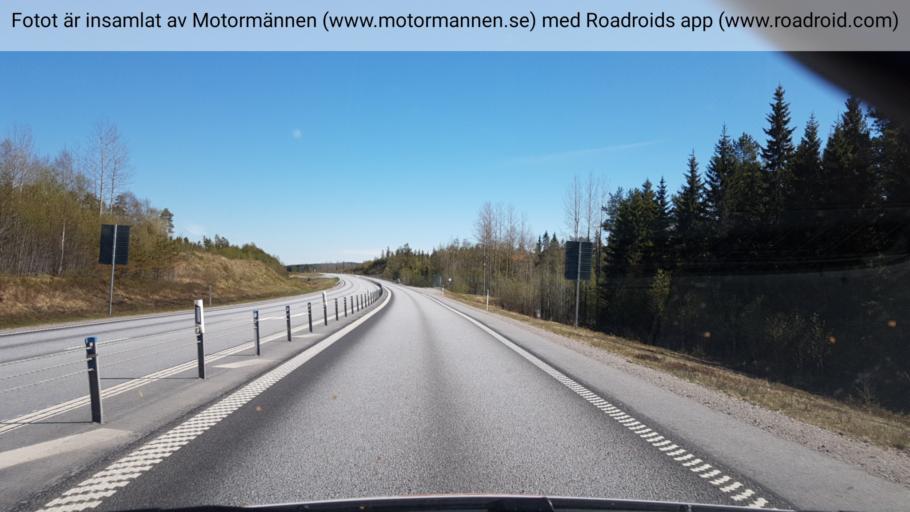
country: SE
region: Vaesterbotten
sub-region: Vannas Kommun
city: Vannasby
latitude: 63.9016
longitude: 19.8984
